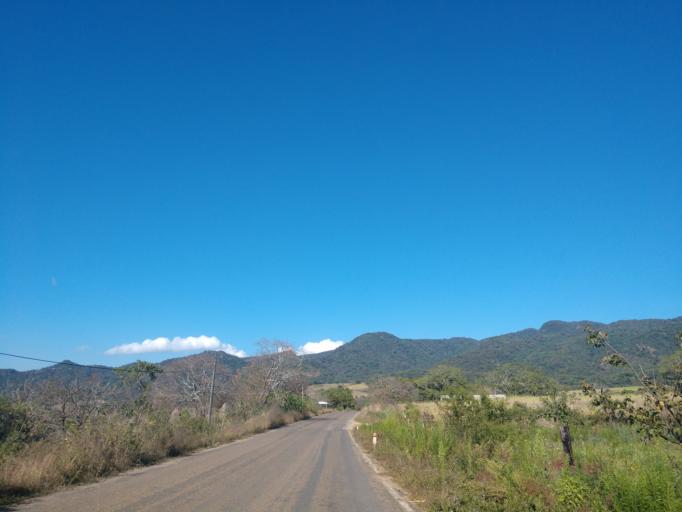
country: MX
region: Nayarit
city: Compostela
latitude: 21.2739
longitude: -104.8834
